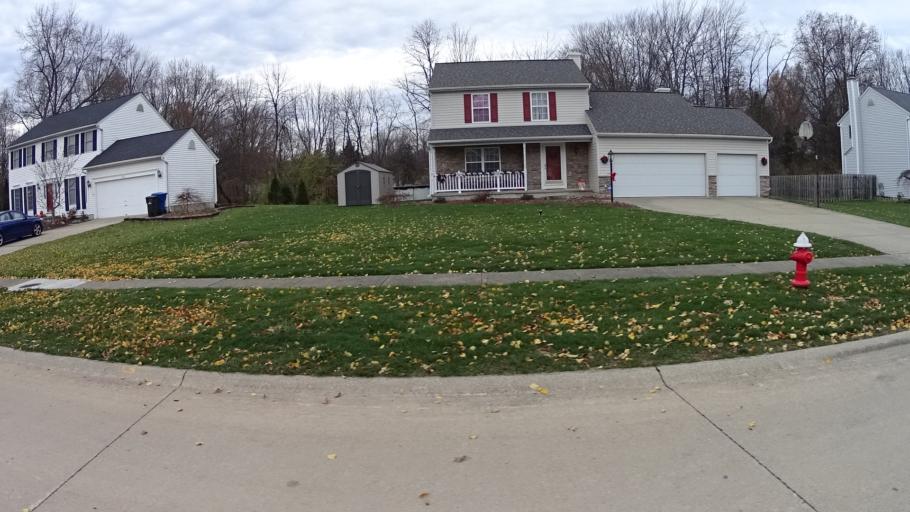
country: US
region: Ohio
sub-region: Lorain County
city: North Ridgeville
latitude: 41.3880
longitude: -82.0092
